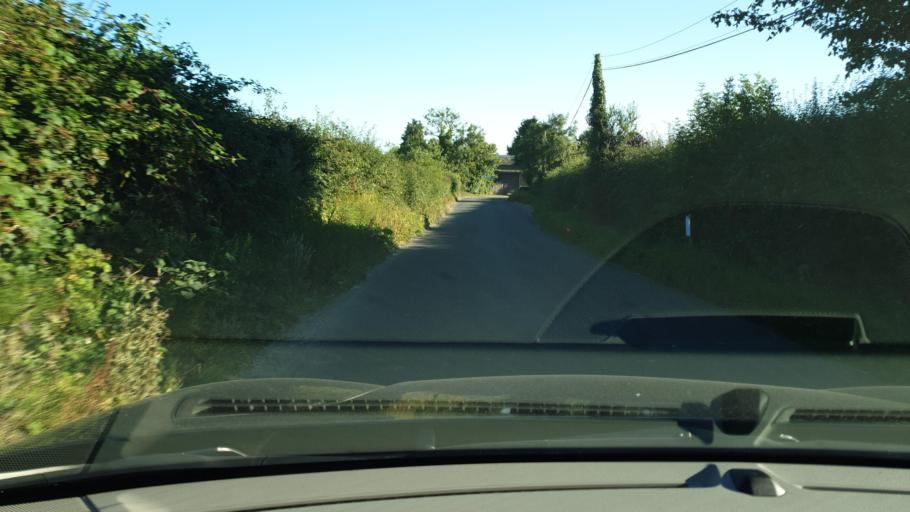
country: IE
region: Leinster
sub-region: An Mhi
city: Ashbourne
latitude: 53.4618
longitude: -6.3811
